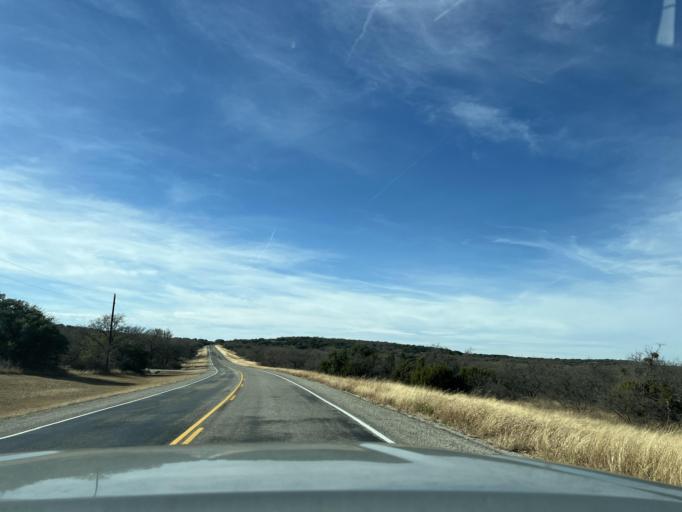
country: US
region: Texas
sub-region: Eastland County
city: Cisco
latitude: 32.4645
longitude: -99.0200
